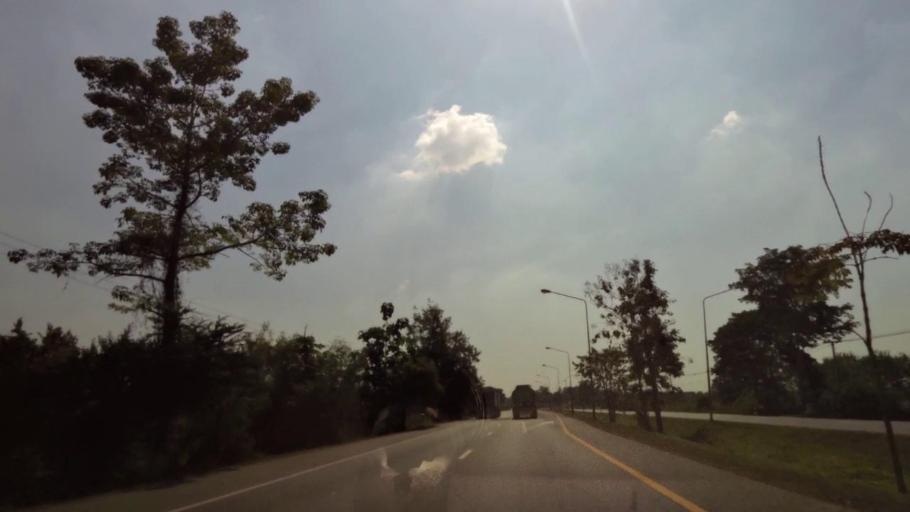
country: TH
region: Phichit
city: Bueng Na Rang
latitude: 16.1632
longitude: 100.1261
